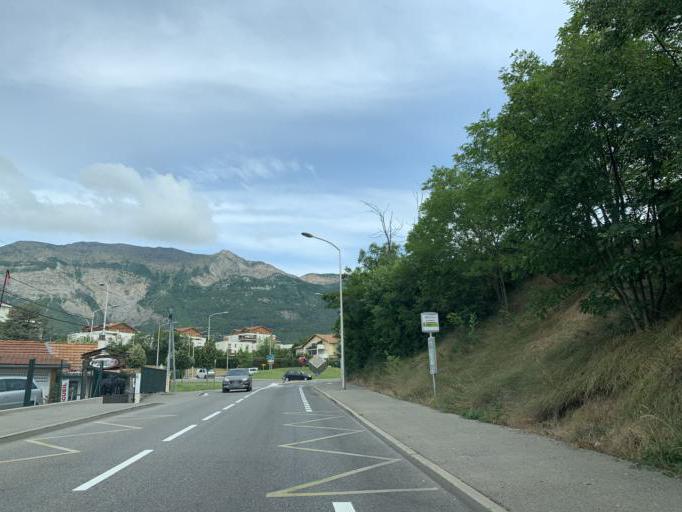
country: FR
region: Provence-Alpes-Cote d'Azur
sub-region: Departement des Hautes-Alpes
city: Gap
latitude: 44.5565
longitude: 6.0643
